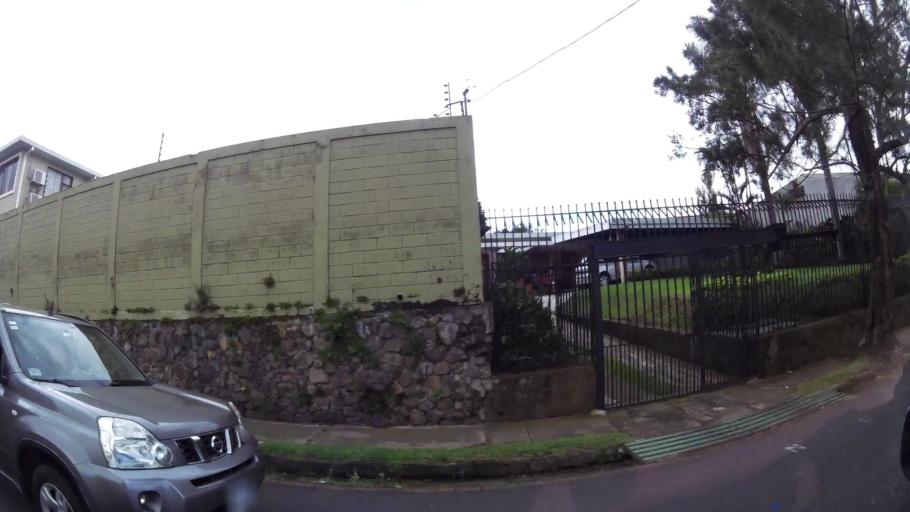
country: CR
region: San Jose
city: San Pedro
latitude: 9.9299
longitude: -84.0503
